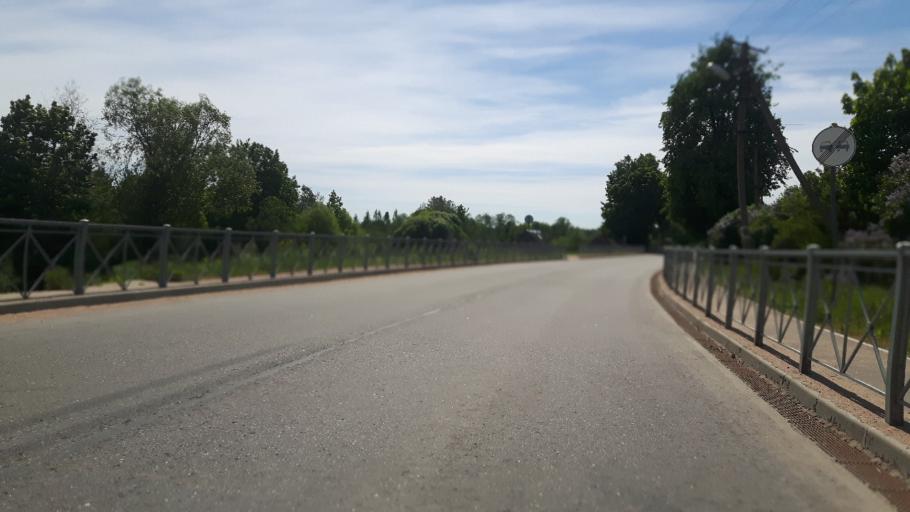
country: RU
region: Leningrad
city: Ust'-Luga
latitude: 59.5872
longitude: 28.1940
